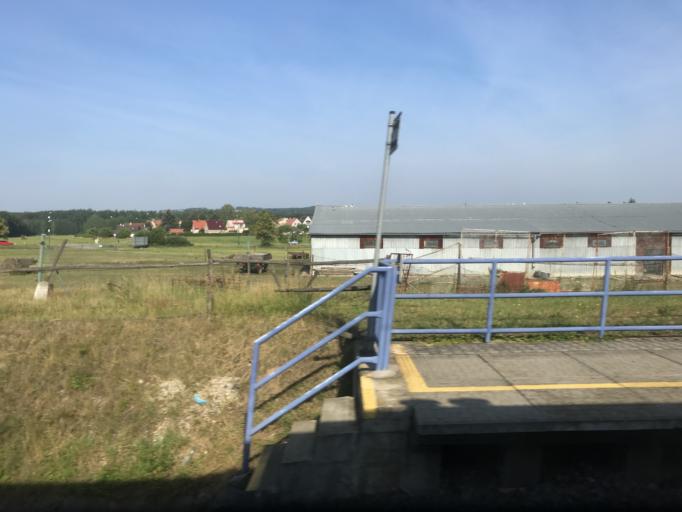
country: CZ
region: Jihocesky
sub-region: Okres Tabor
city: Sezimovo Usti
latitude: 49.3783
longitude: 14.6968
